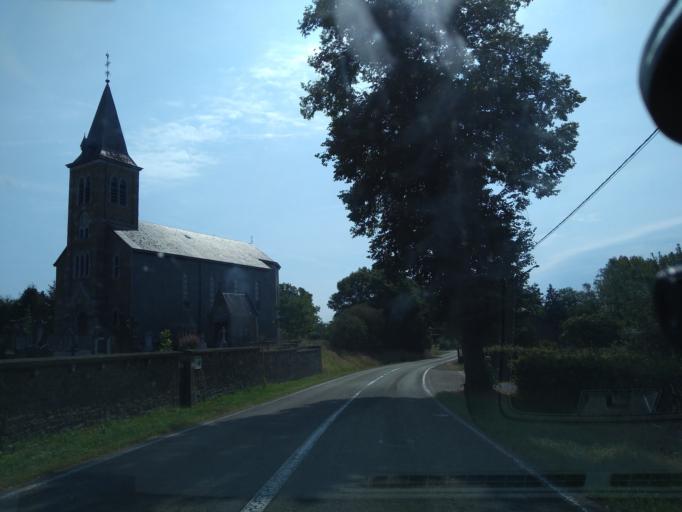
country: BE
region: Wallonia
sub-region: Province du Luxembourg
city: La Roche-en-Ardenne
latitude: 50.1696
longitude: 5.5520
